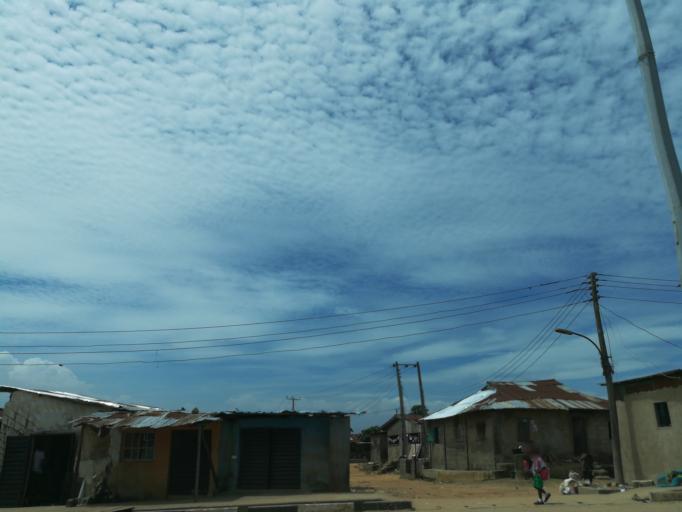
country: NG
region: Lagos
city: Ebute Ikorodu
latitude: 6.5530
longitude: 3.4736
